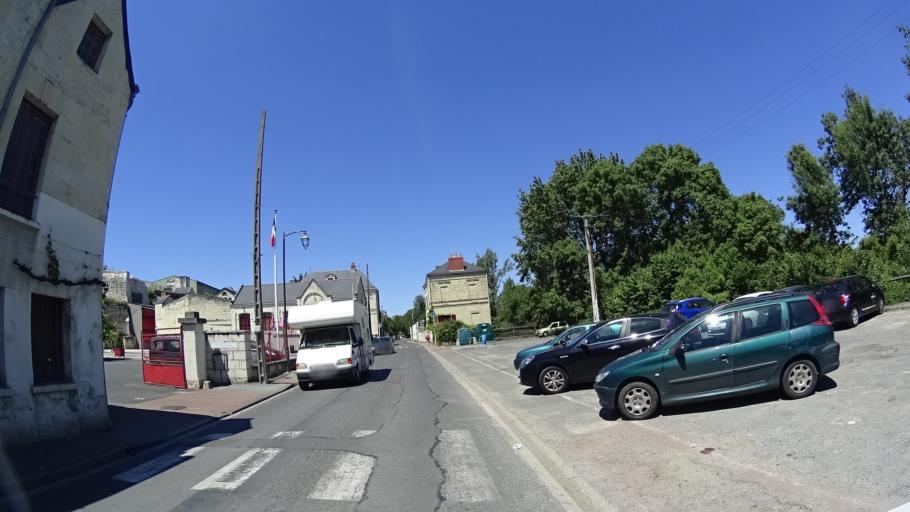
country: FR
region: Pays de la Loire
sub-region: Departement de Maine-et-Loire
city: Saumur
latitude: 47.2703
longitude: -0.1043
